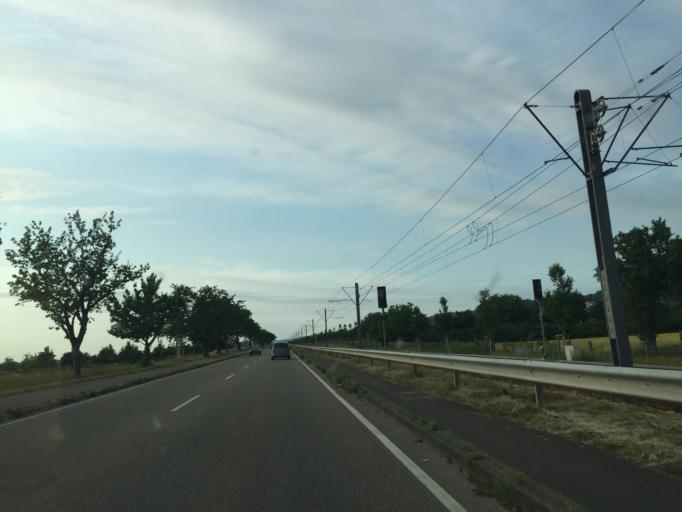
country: DE
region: Baden-Wuerttemberg
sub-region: Karlsruhe Region
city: Schriesheim
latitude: 49.4836
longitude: 8.6570
